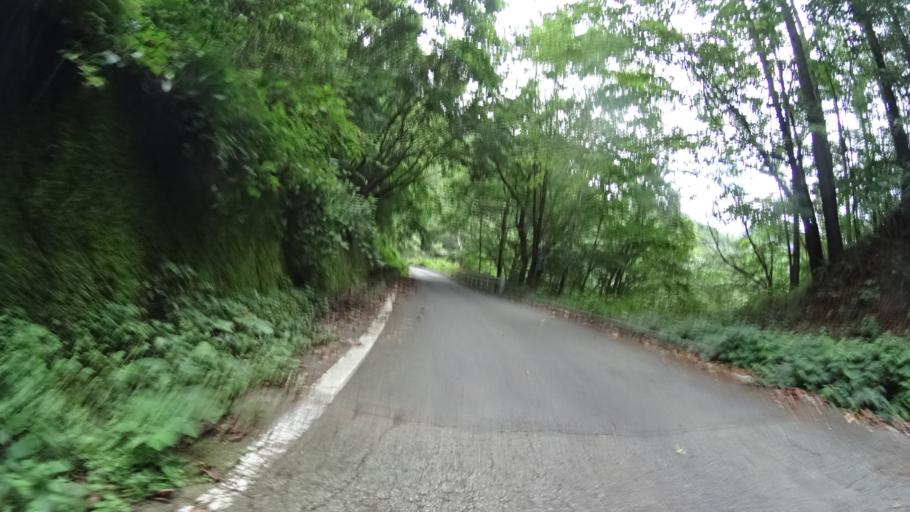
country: JP
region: Yamanashi
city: Nirasaki
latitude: 35.8079
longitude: 138.5471
